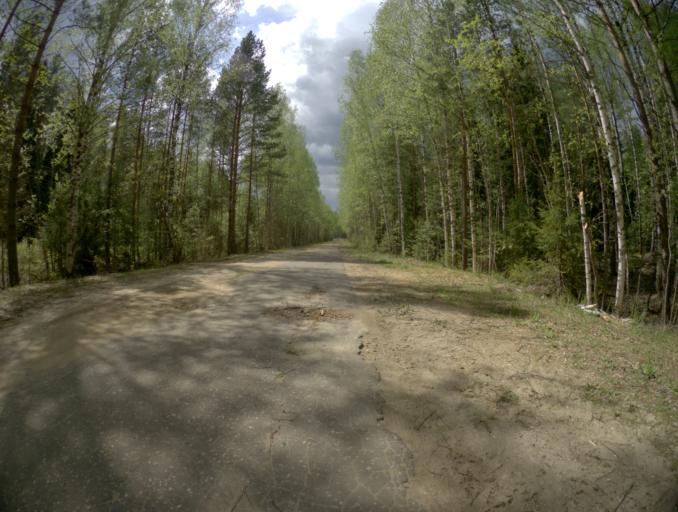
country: RU
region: Vladimir
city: Velikodvorskiy
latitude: 55.2449
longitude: 40.7489
